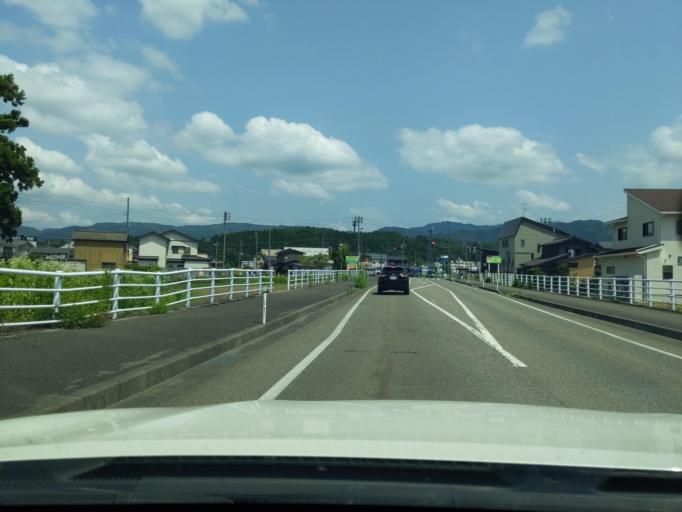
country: JP
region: Niigata
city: Nagaoka
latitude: 37.4268
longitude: 138.8607
